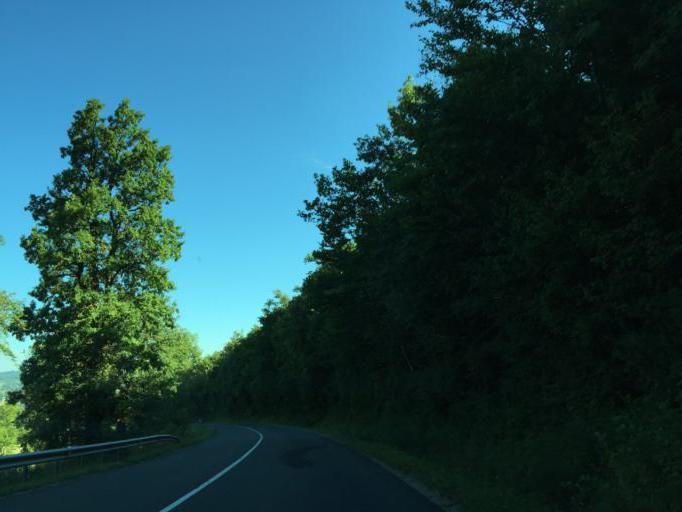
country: FR
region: Midi-Pyrenees
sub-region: Departement de l'Aveyron
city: Laissac
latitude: 44.4324
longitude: 2.7988
